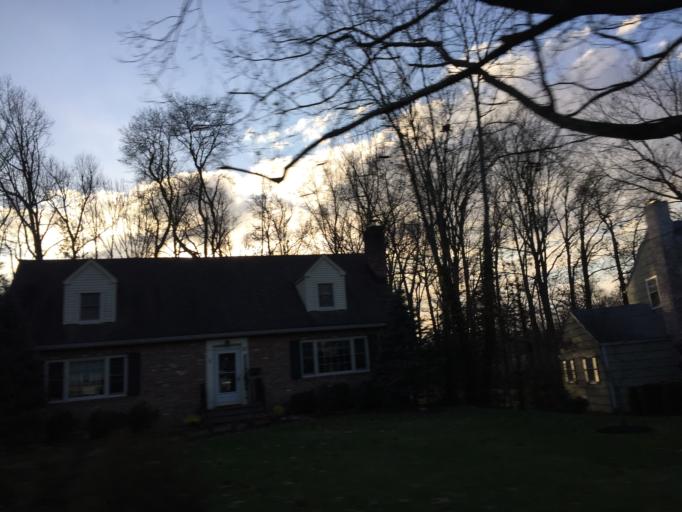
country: US
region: New Jersey
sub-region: Union County
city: Summit
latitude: 40.7252
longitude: -74.3673
